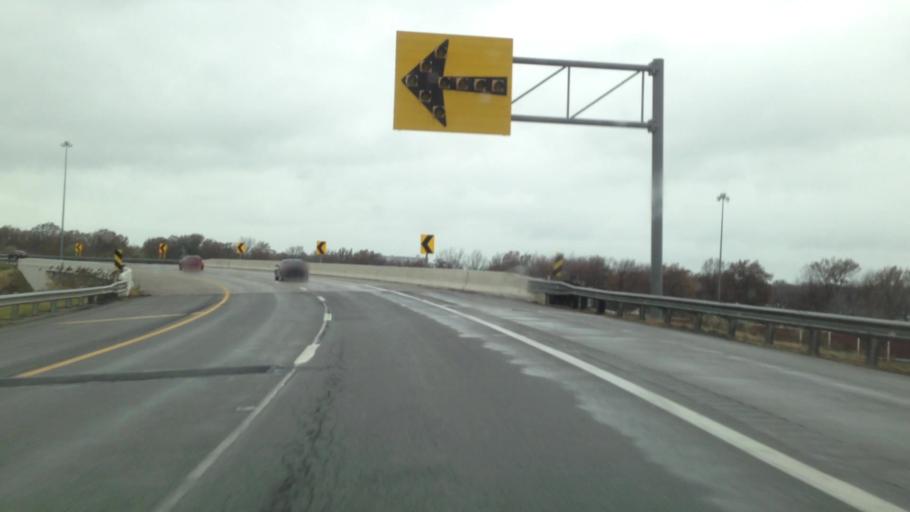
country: US
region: Ohio
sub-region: Cuyahoga County
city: Euclid
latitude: 41.6052
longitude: -81.4934
